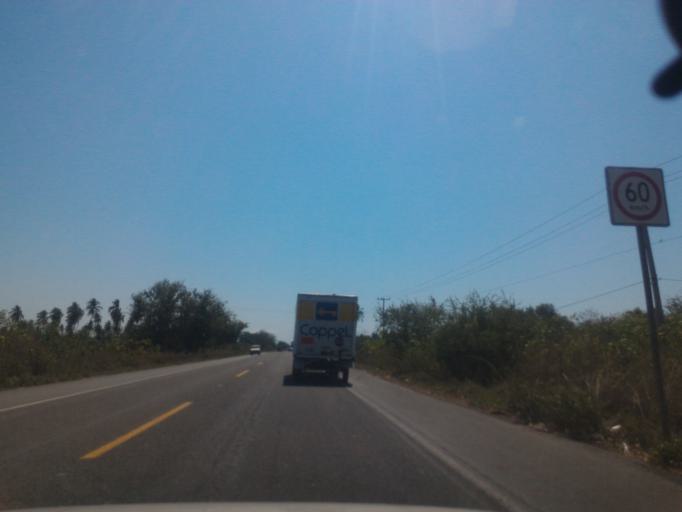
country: MX
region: Colima
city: Tecoman
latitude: 18.8428
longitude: -103.8239
